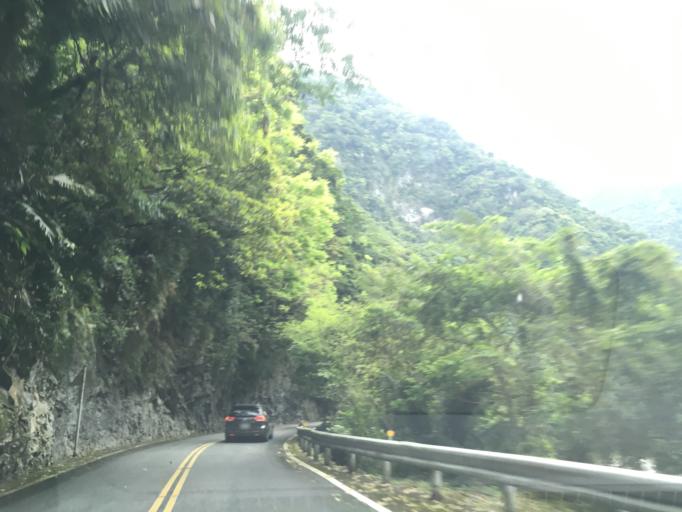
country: TW
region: Taiwan
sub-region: Hualien
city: Hualian
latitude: 24.1601
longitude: 121.6152
